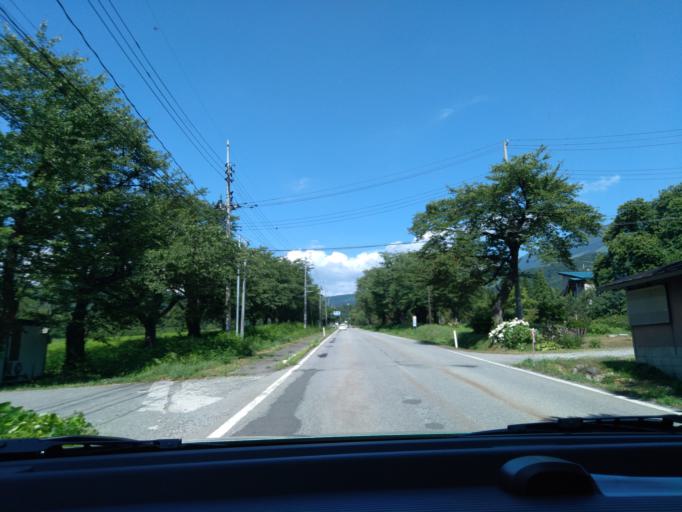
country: JP
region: Akita
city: Kakunodatemachi
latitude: 39.7538
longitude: 140.7285
